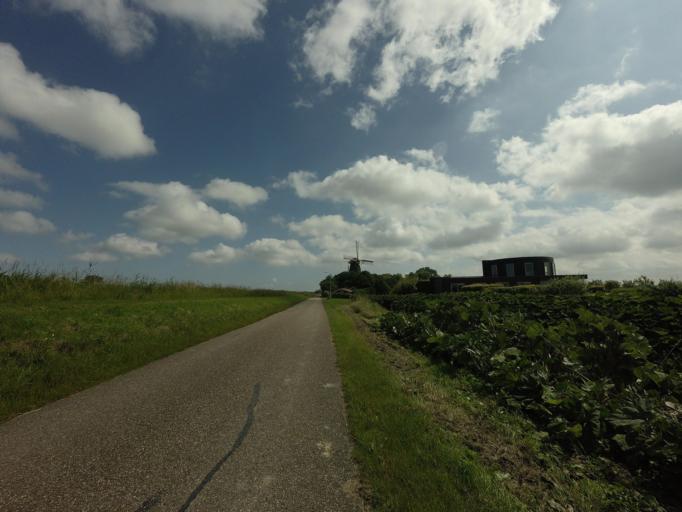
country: NL
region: North Holland
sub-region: Gemeente Schagen
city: Schagen
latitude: 52.8551
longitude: 4.8328
